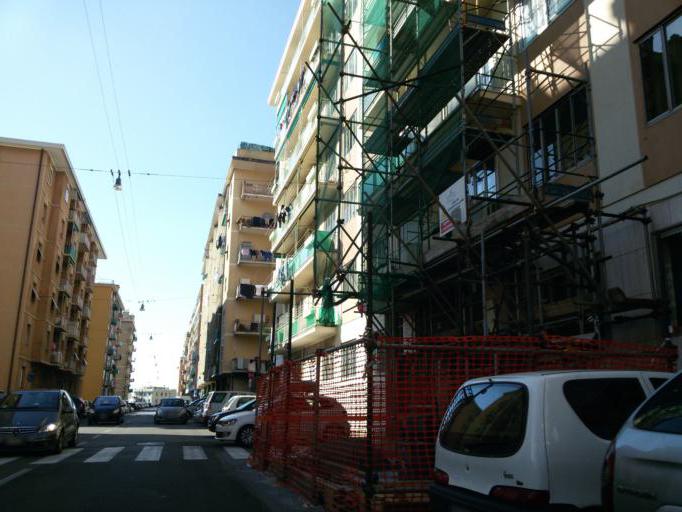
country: IT
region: Liguria
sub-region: Provincia di Genova
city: Genoa
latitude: 44.4233
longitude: 8.9163
